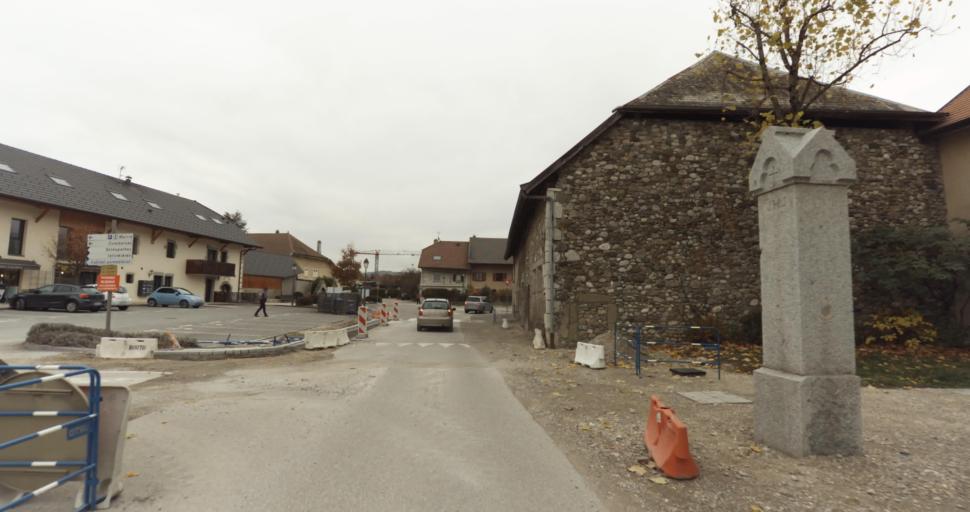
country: FR
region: Rhone-Alpes
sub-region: Departement de la Haute-Savoie
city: Metz-Tessy
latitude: 45.9394
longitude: 6.1061
